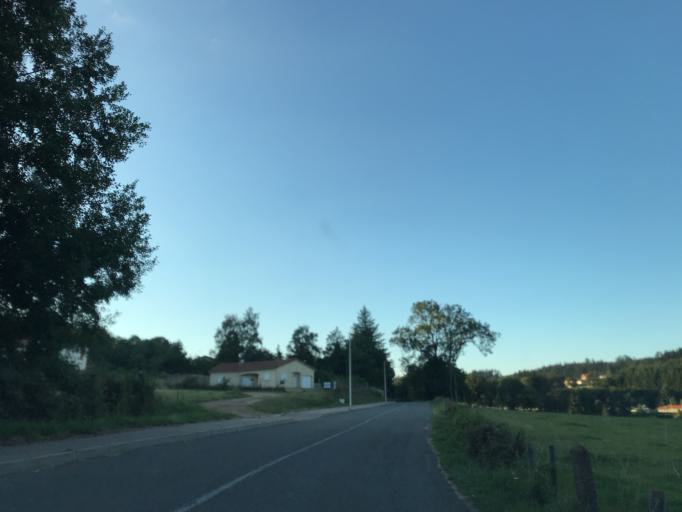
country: FR
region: Rhone-Alpes
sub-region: Departement de la Loire
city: Noiretable
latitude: 45.8090
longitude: 3.7689
